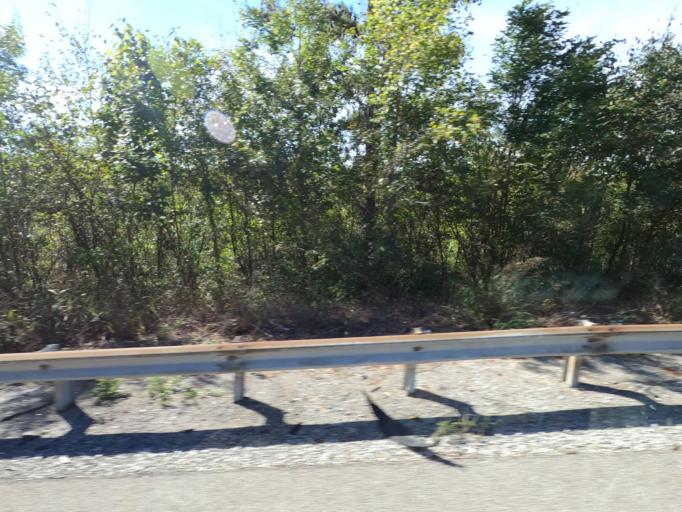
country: US
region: Tennessee
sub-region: Dickson County
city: Burns
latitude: 36.0190
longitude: -87.2550
